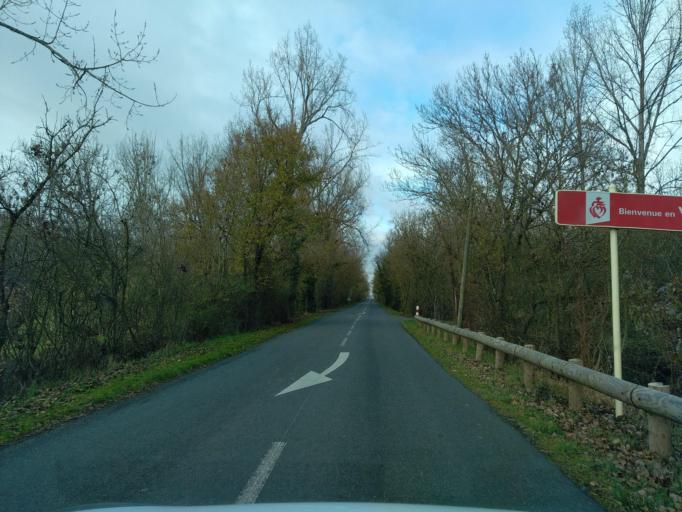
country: FR
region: Pays de la Loire
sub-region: Departement de la Vendee
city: Vix
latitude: 46.3376
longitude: -0.8254
